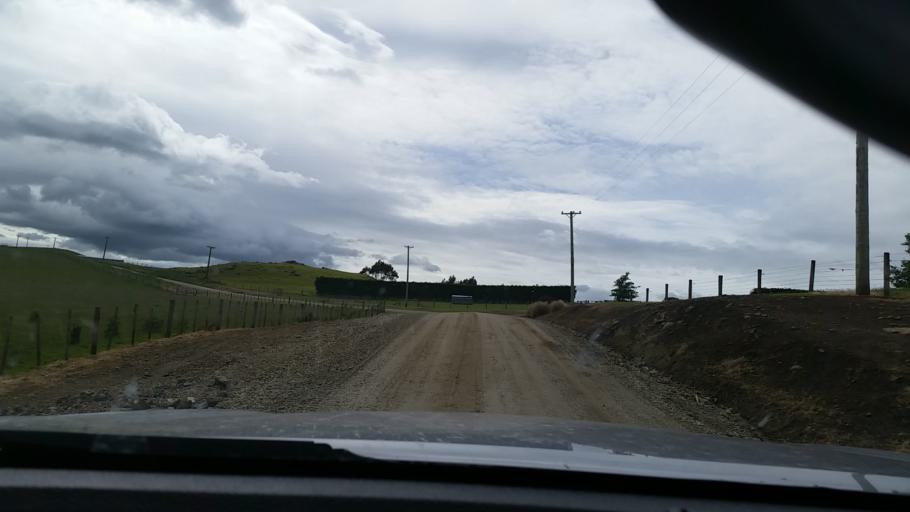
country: NZ
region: Southland
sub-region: Gore District
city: Gore
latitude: -46.2611
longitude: 168.9270
